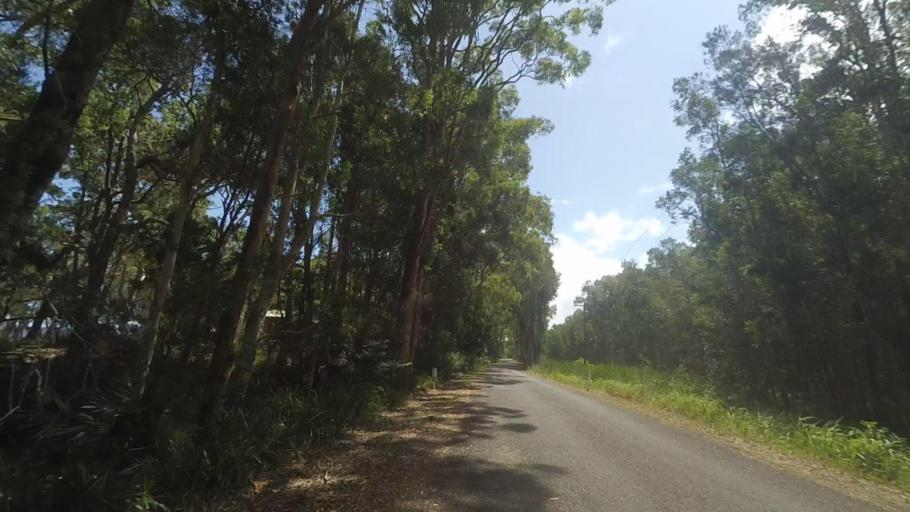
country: AU
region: New South Wales
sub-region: Great Lakes
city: Bulahdelah
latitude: -32.5085
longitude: 152.2994
